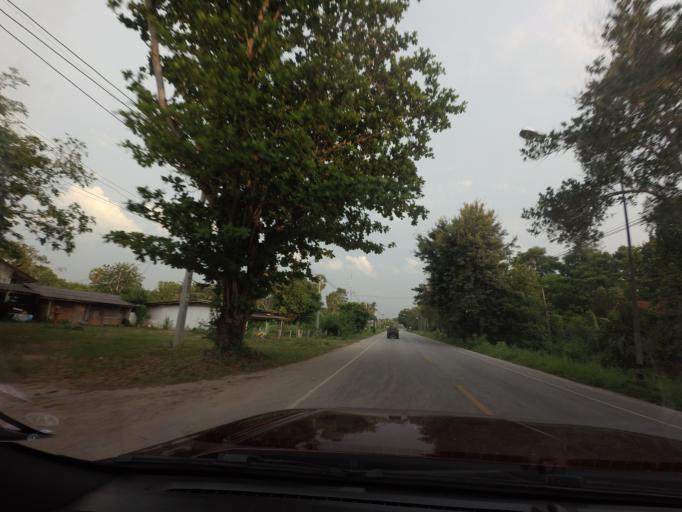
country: TH
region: Pattani
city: Mae Lan
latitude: 6.6352
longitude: 101.1861
